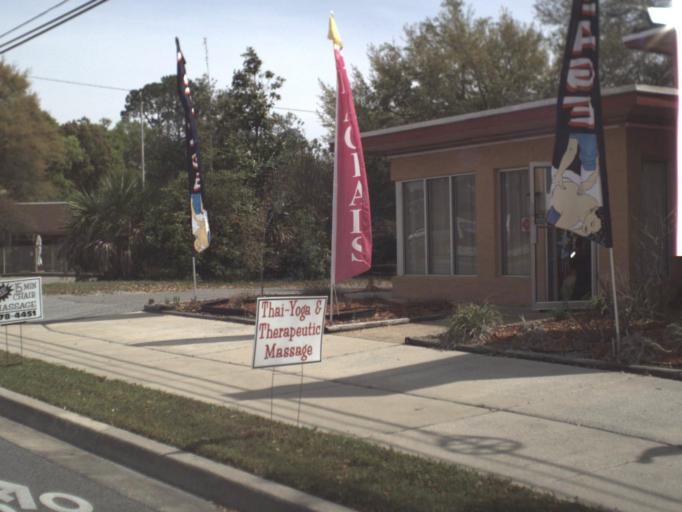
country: US
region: Florida
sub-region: Okaloosa County
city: Niceville
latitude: 30.5225
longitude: -86.4954
